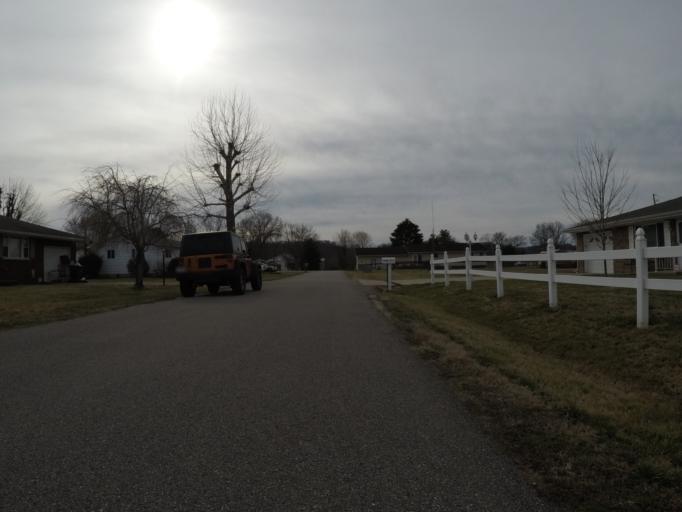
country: US
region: West Virginia
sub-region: Cabell County
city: Pea Ridge
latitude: 38.4470
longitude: -82.3543
